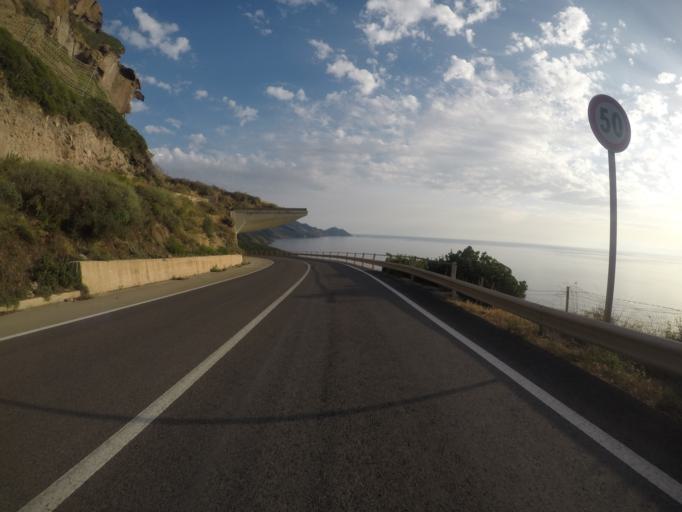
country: IT
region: Sardinia
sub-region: Provincia di Sassari
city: Villanova Monteleone
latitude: 40.4421
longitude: 8.3954
